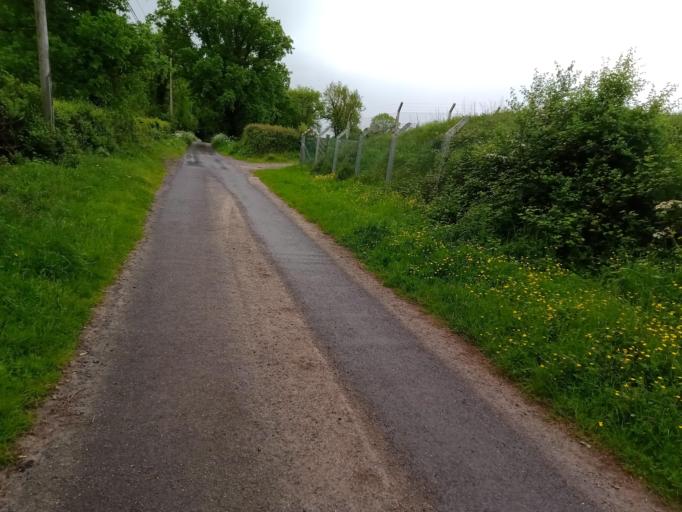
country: IE
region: Leinster
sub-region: Kilkenny
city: Thomastown
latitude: 52.5132
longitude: -7.1330
